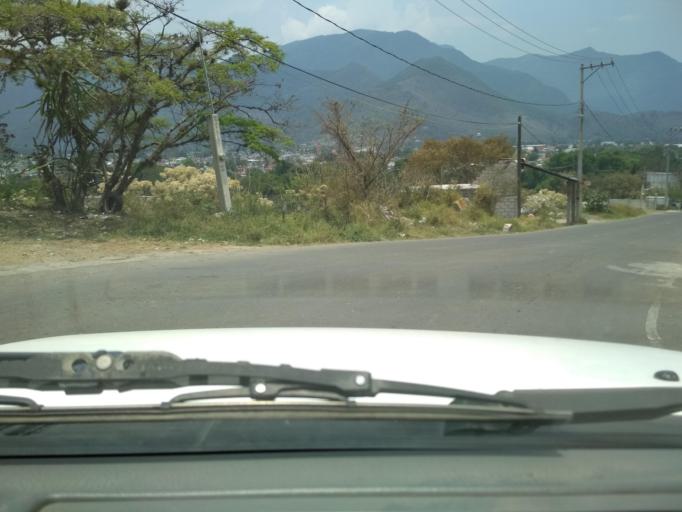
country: MX
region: Veracruz
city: Ciudad Mendoza
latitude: 18.7937
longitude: -97.1805
